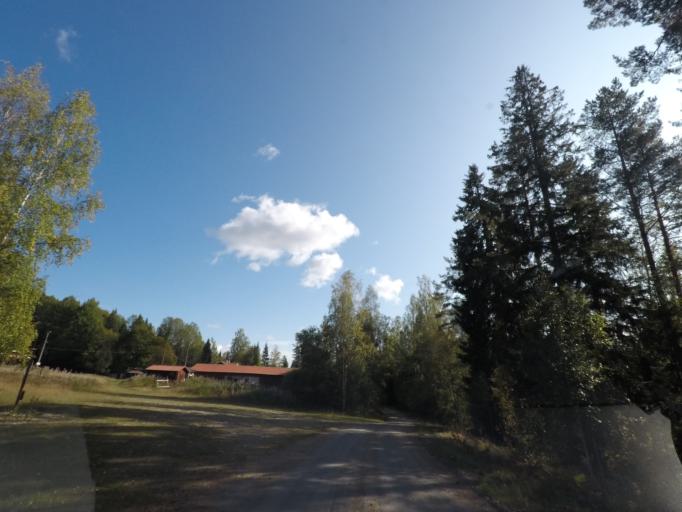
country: SE
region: Vaestmanland
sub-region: Skinnskattebergs Kommun
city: Skinnskatteberg
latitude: 59.8294
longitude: 15.5118
